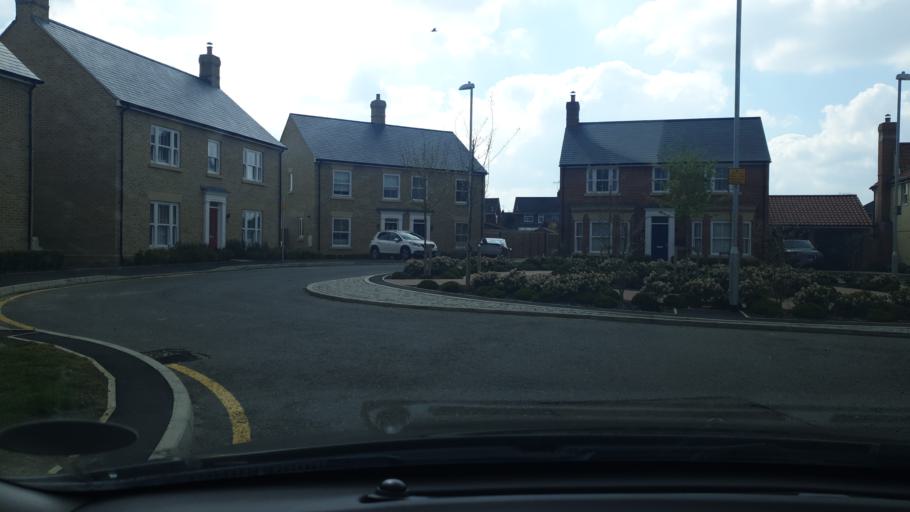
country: GB
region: England
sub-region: Essex
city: Manningtree
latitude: 51.9415
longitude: 1.0478
